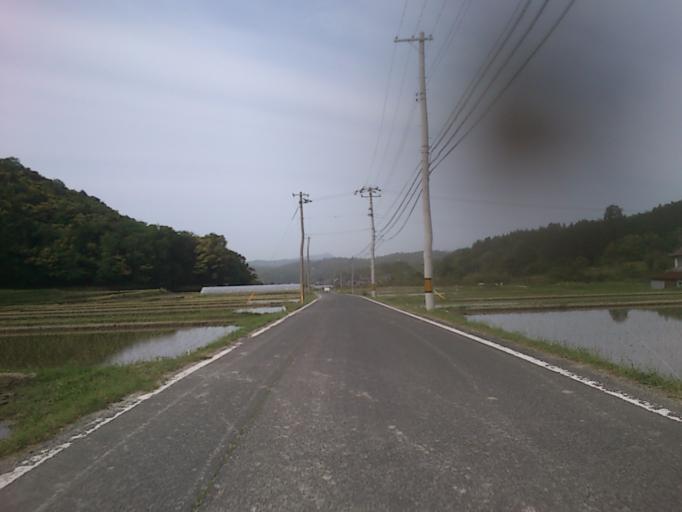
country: JP
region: Kyoto
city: Miyazu
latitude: 35.6410
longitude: 135.0201
